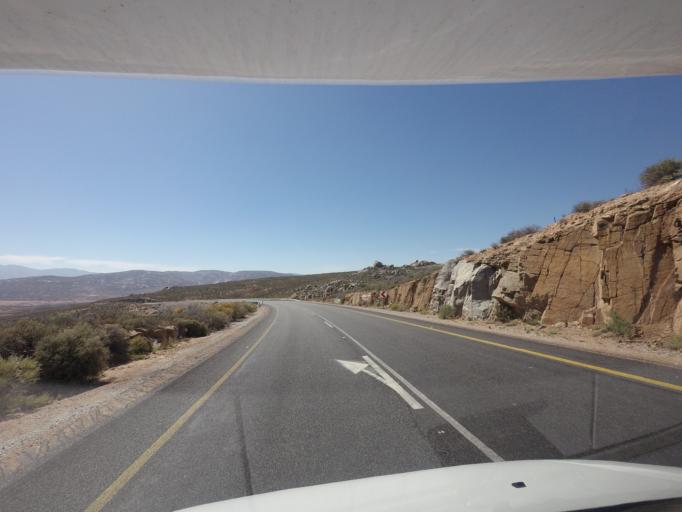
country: ZA
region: Northern Cape
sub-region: Namakwa District Municipality
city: Garies
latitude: -30.5489
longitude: 17.9621
